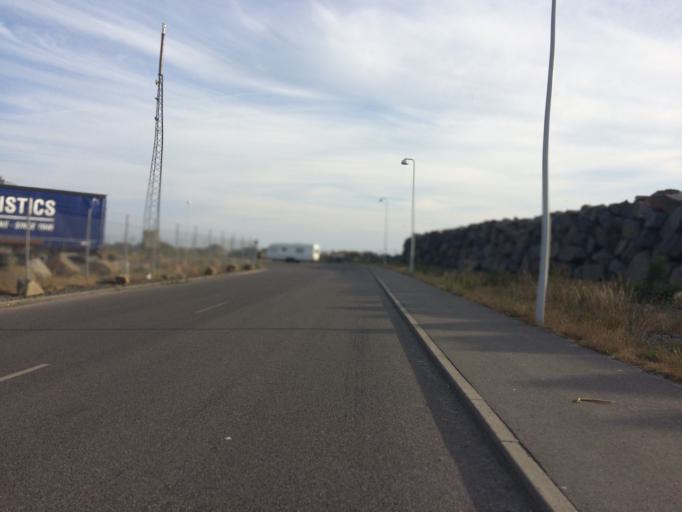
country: DK
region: Capital Region
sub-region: Bornholm Kommune
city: Ronne
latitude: 55.1018
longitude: 14.6852
